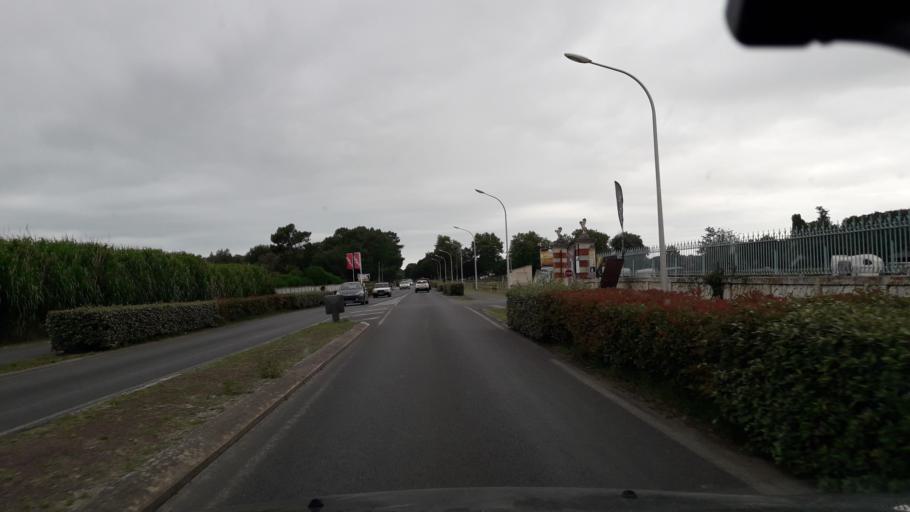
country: FR
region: Poitou-Charentes
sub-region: Departement de la Charente-Maritime
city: Les Mathes
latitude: 45.7030
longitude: -1.1679
